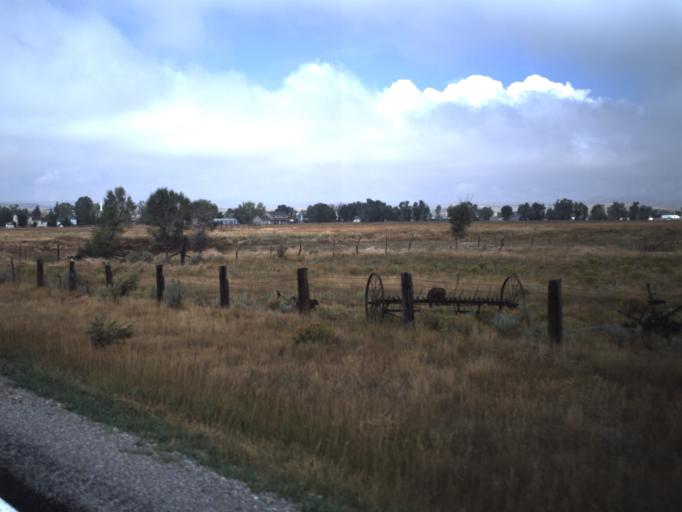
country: US
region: Utah
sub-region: Rich County
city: Randolph
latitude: 41.5174
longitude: -111.1536
